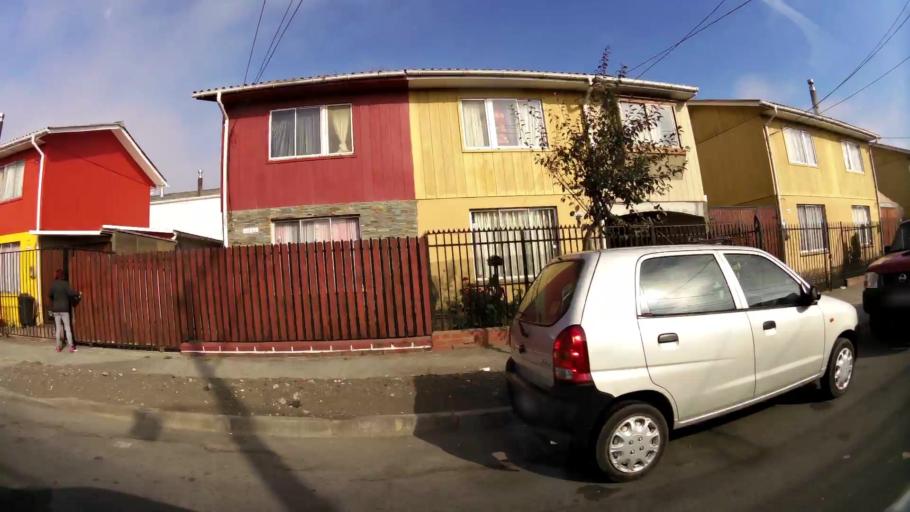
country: CL
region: Biobio
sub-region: Provincia de Concepcion
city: Concepcion
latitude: -36.7967
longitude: -73.1123
